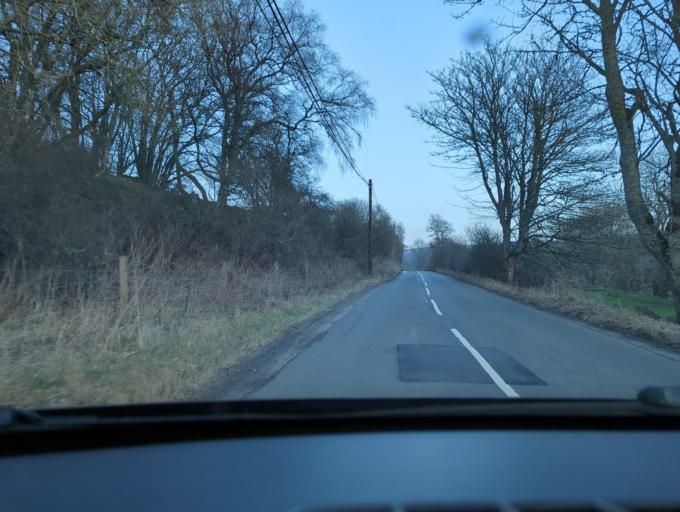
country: GB
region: Scotland
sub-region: Perth and Kinross
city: Methven
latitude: 56.5381
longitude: -3.6914
